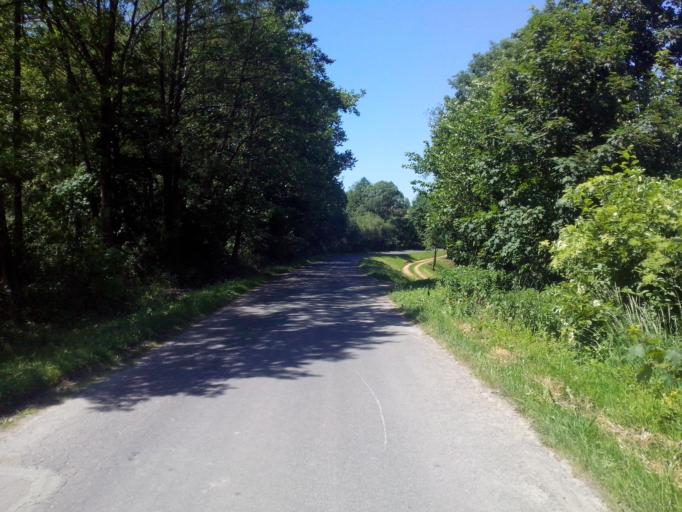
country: PL
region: Subcarpathian Voivodeship
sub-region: Powiat krosnienski
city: Wojaszowka
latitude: 49.7972
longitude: 21.7044
